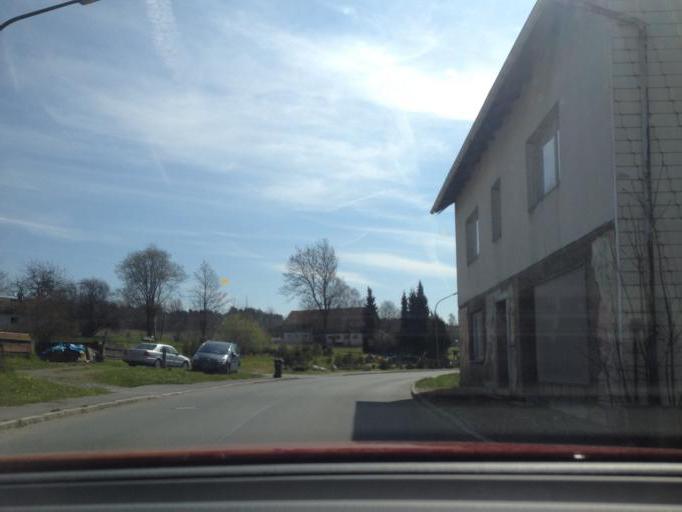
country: DE
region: Bavaria
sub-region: Upper Franconia
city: Oberhaid
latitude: 50.0959
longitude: 11.7912
